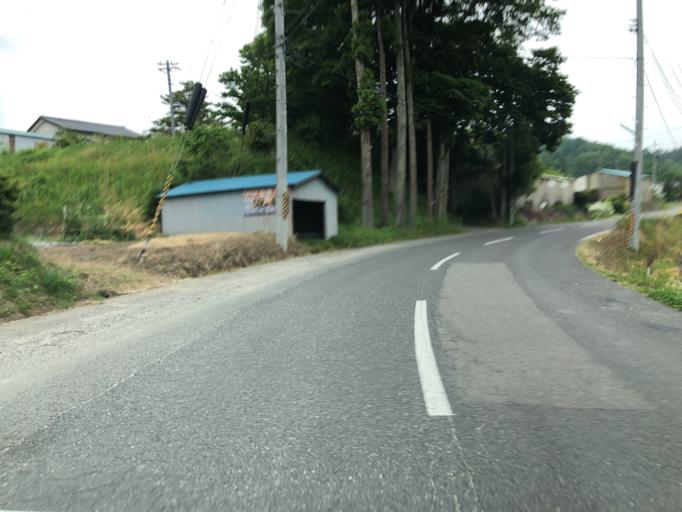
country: JP
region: Fukushima
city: Funehikimachi-funehiki
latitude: 37.4249
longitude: 140.6052
